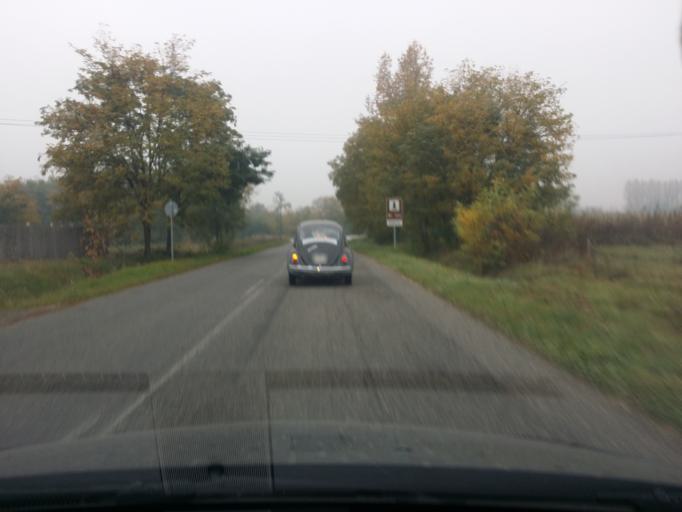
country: HU
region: Szabolcs-Szatmar-Bereg
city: Nyirbogdany
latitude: 48.0608
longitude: 21.8596
